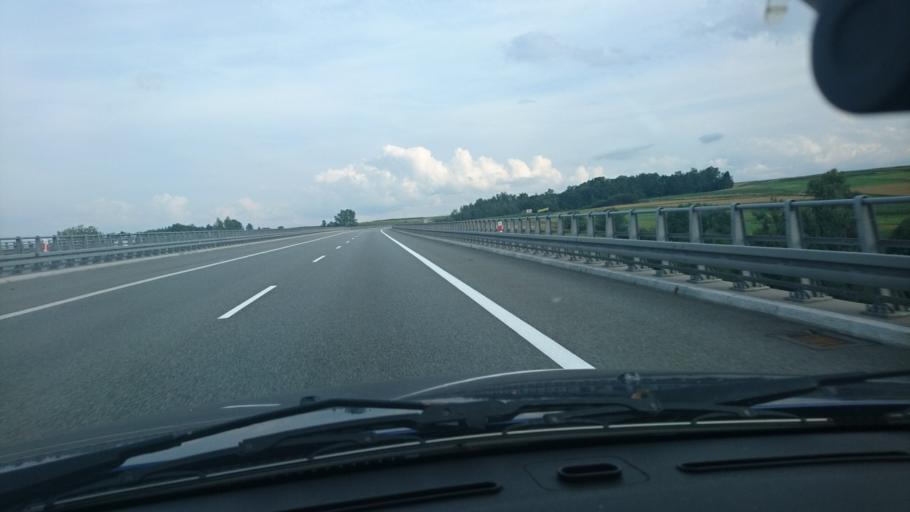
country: PL
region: Silesian Voivodeship
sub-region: Powiat zywiecki
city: Lesna
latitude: 49.6990
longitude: 19.1305
